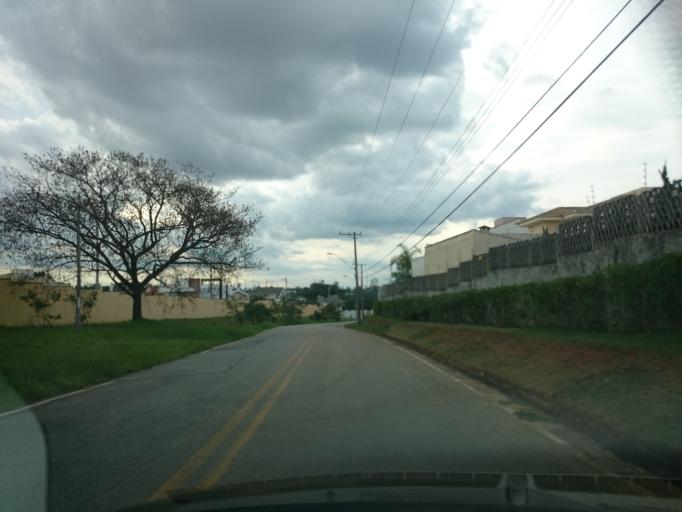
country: BR
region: Sao Paulo
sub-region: Sorocaba
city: Sorocaba
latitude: -23.4769
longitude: -47.4047
